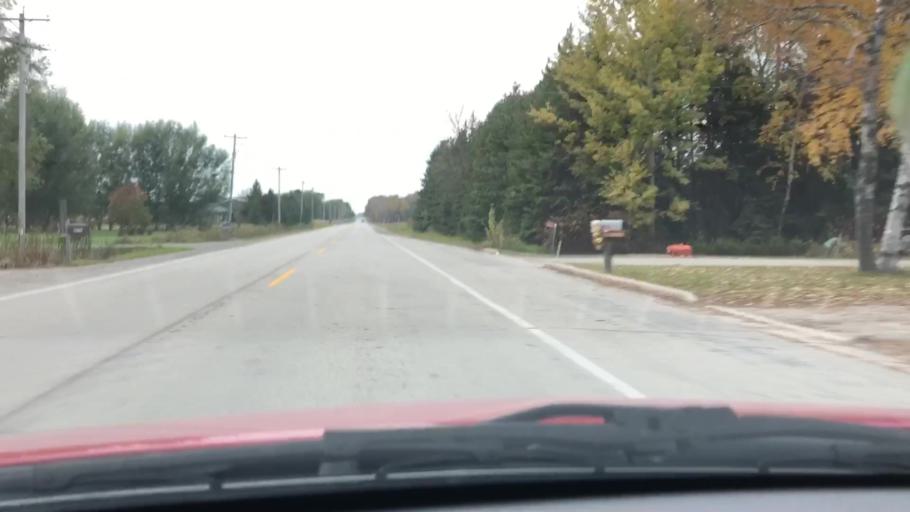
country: US
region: Wisconsin
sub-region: Brown County
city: Oneida
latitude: 44.4442
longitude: -88.2087
